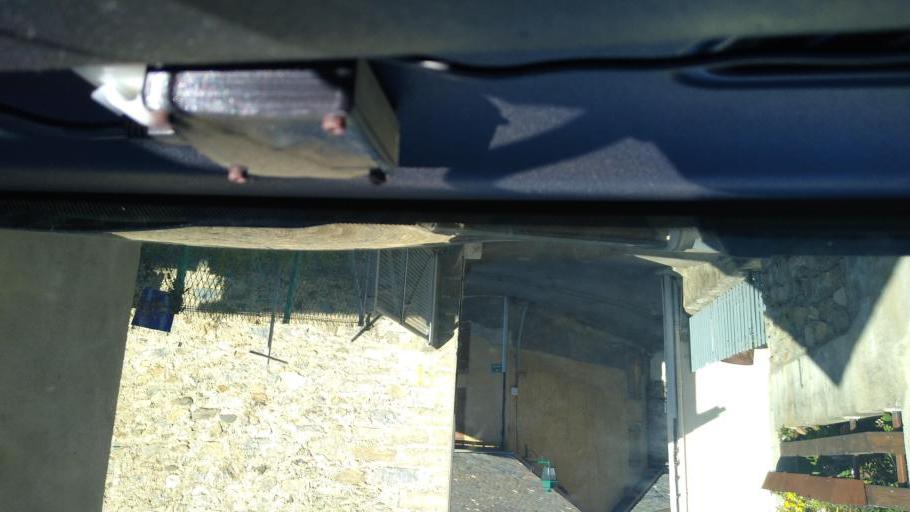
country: FR
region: Languedoc-Roussillon
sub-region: Departement de l'Aude
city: Quillan
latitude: 42.7312
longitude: 2.0700
